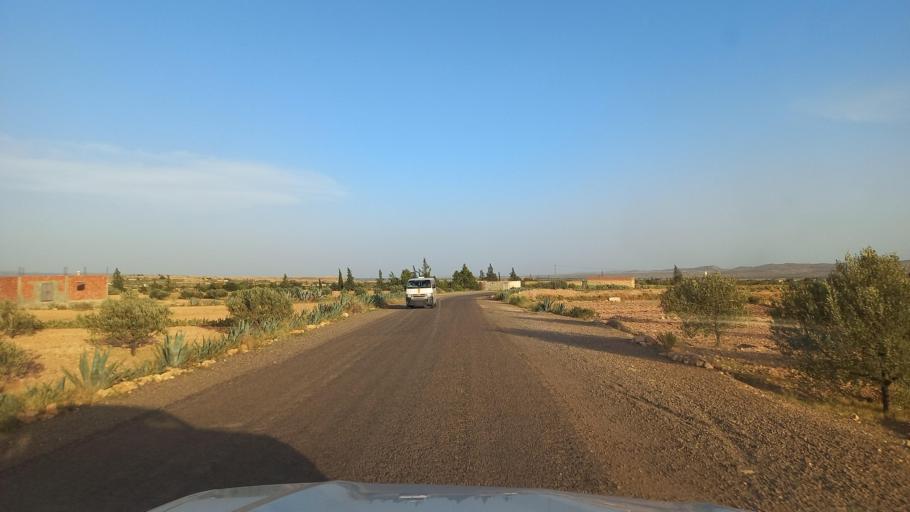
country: TN
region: Al Qasrayn
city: Kasserine
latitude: 35.2719
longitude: 8.9271
